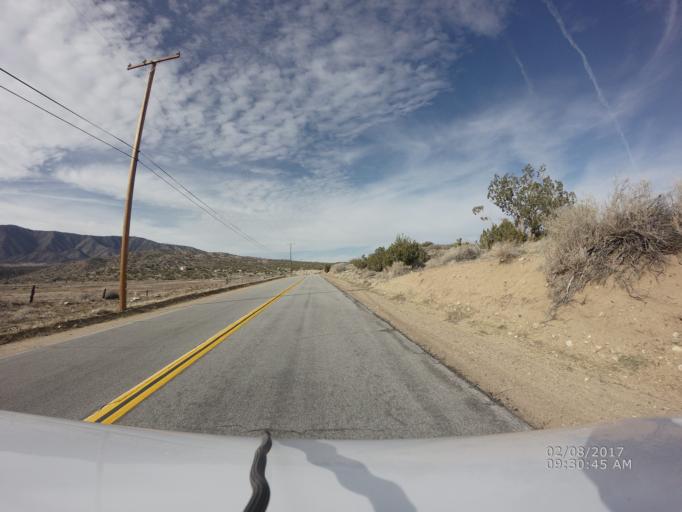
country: US
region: California
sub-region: Los Angeles County
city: Littlerock
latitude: 34.4577
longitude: -117.8971
